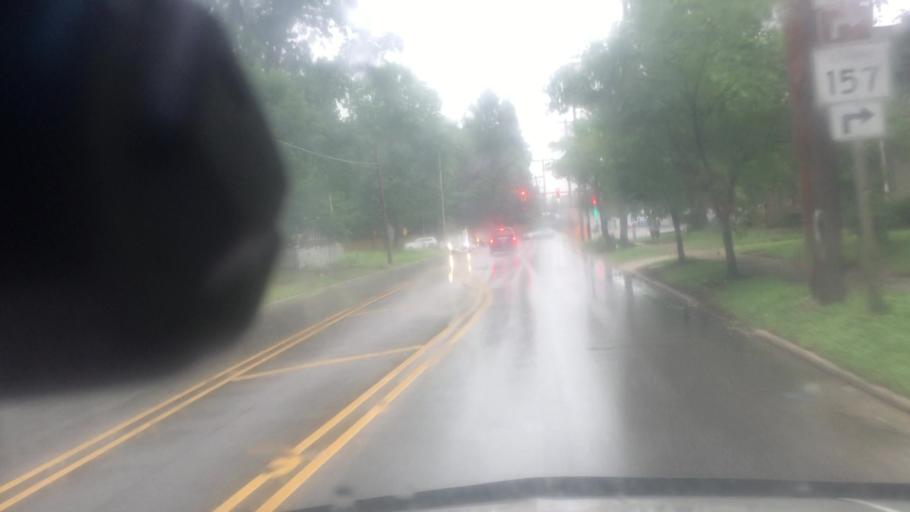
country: US
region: Illinois
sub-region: Madison County
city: Edwardsville
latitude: 38.8138
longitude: -89.9475
